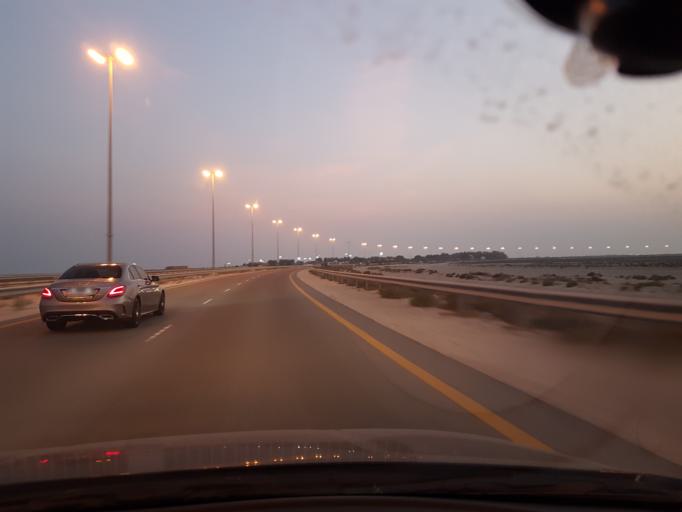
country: BH
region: Central Governorate
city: Dar Kulayb
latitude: 25.9981
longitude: 50.4845
